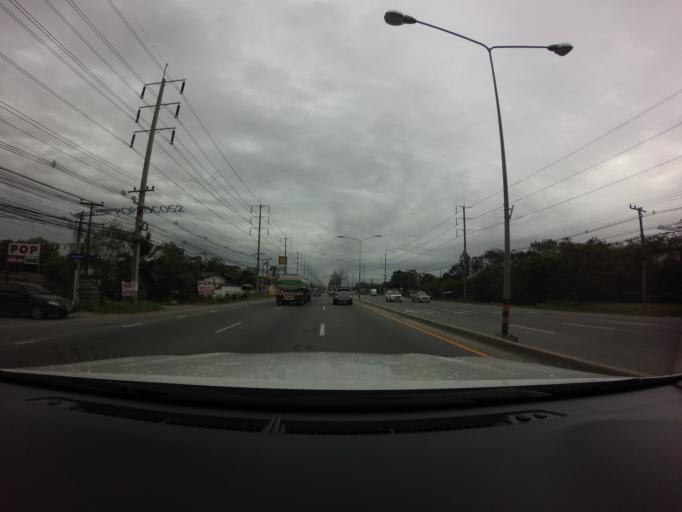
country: TH
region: Chachoengsao
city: Bang Pakong
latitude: 13.5796
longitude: 101.0065
